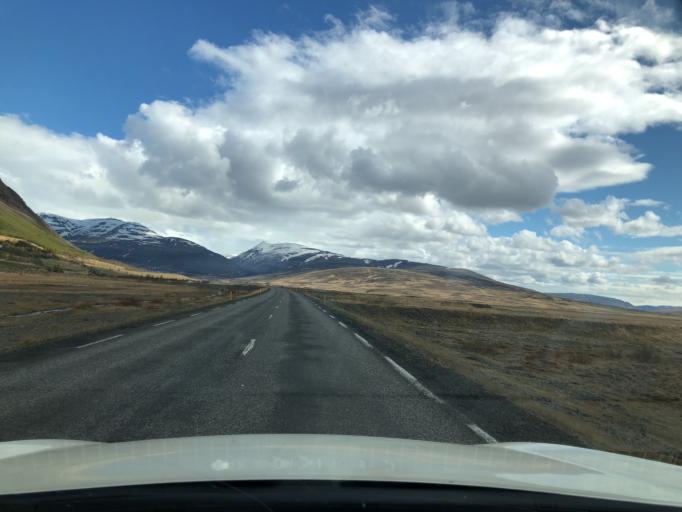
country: IS
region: Northwest
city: Saudarkrokur
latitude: 65.4393
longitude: -19.1906
